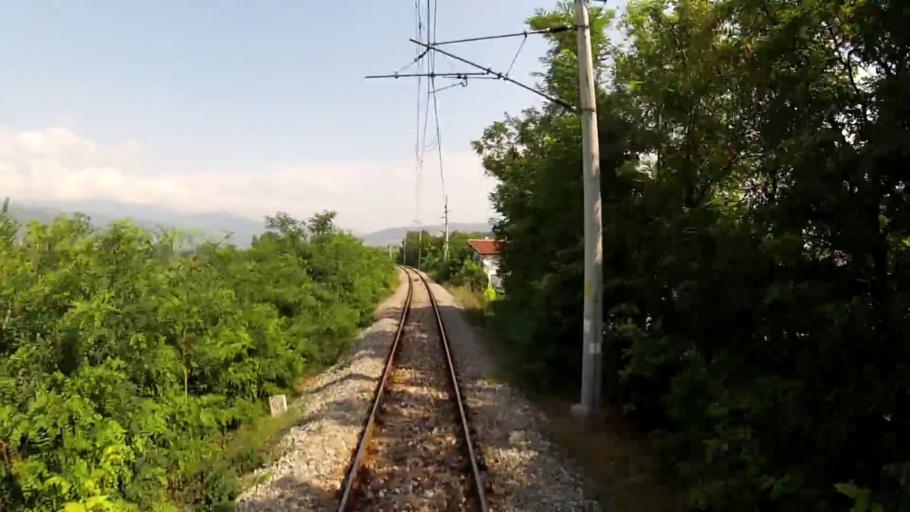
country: BG
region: Blagoevgrad
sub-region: Obshtina Strumyani
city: Strumyani
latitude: 41.6593
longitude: 23.1783
